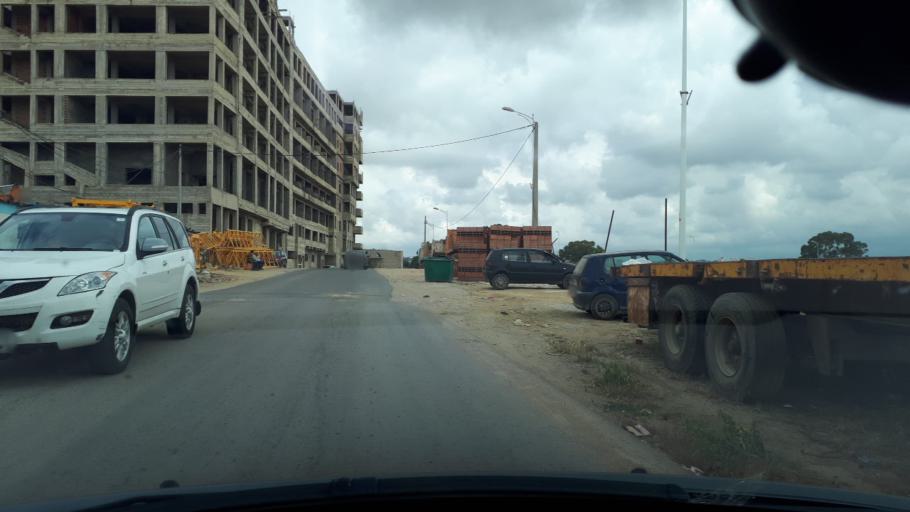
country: DZ
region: Tipaza
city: Cheraga
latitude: 36.7385
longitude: 2.9061
